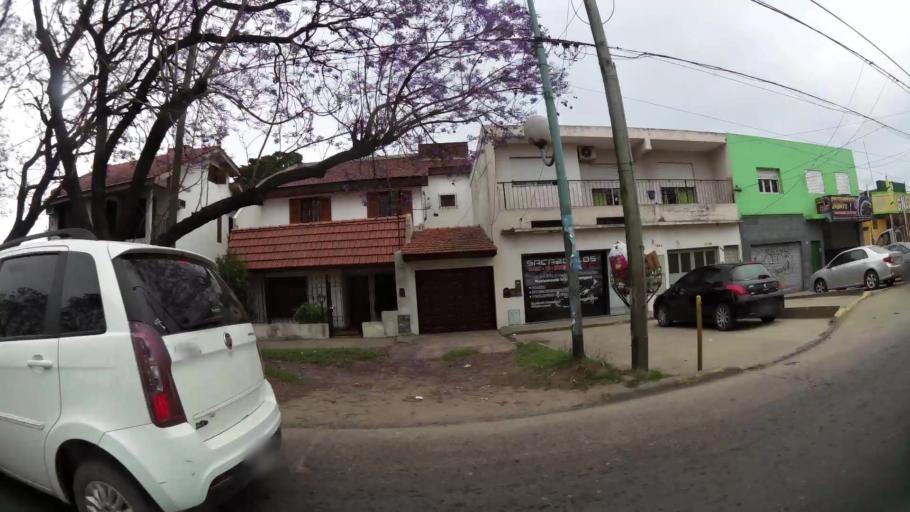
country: AR
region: Buenos Aires
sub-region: Partido de Zarate
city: Zarate
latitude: -34.1100
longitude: -59.0208
